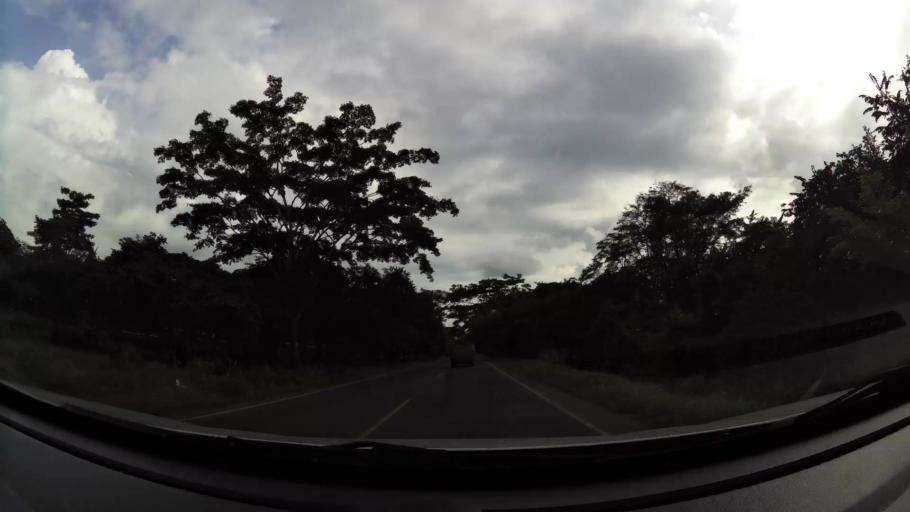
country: CR
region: Guanacaste
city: Juntas
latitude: 10.2300
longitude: -84.9798
